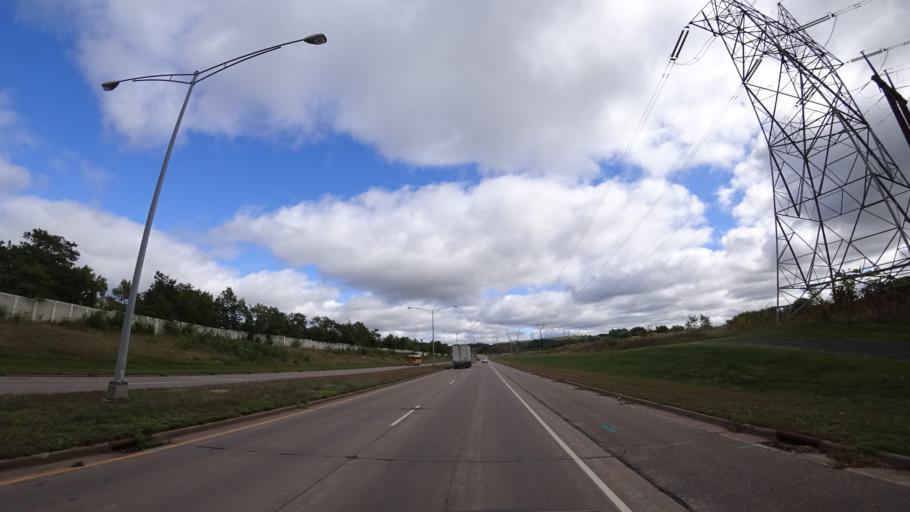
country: US
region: Wisconsin
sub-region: Eau Claire County
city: Eau Claire
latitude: 44.8409
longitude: -91.4954
